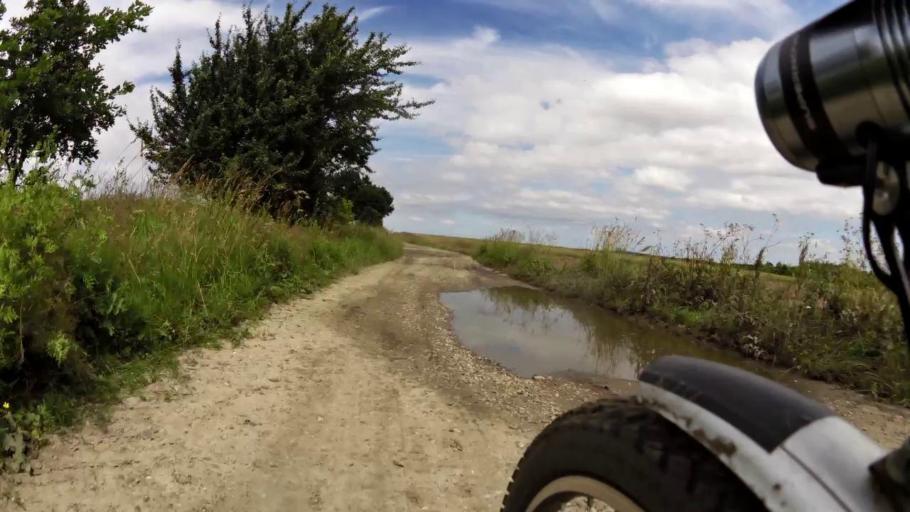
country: PL
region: West Pomeranian Voivodeship
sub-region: Powiat bialogardzki
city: Bialogard
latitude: 53.9697
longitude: 15.9962
